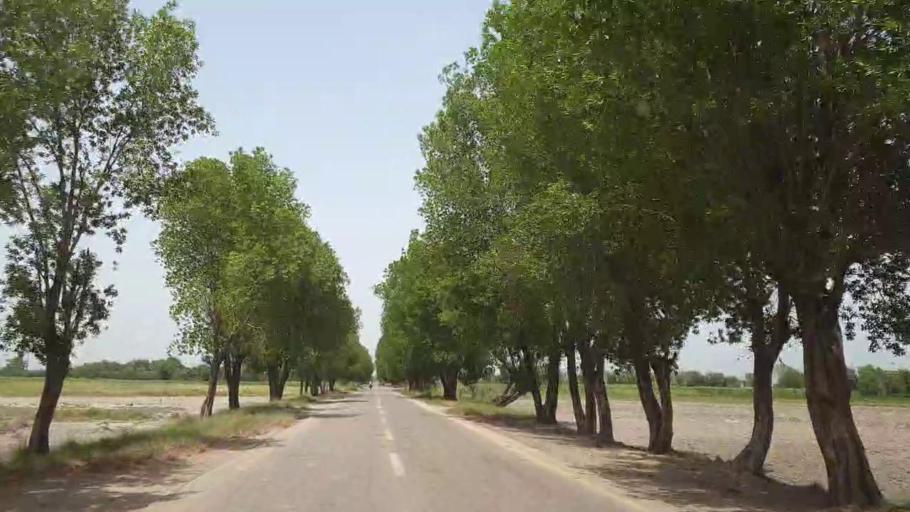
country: PK
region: Sindh
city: Sakrand
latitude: 26.1866
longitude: 68.2327
